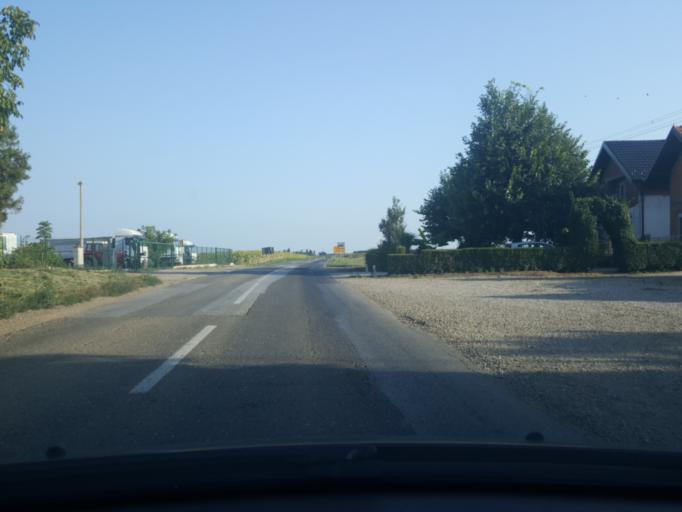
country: RS
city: Hrtkovci
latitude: 44.8683
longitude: 19.7707
